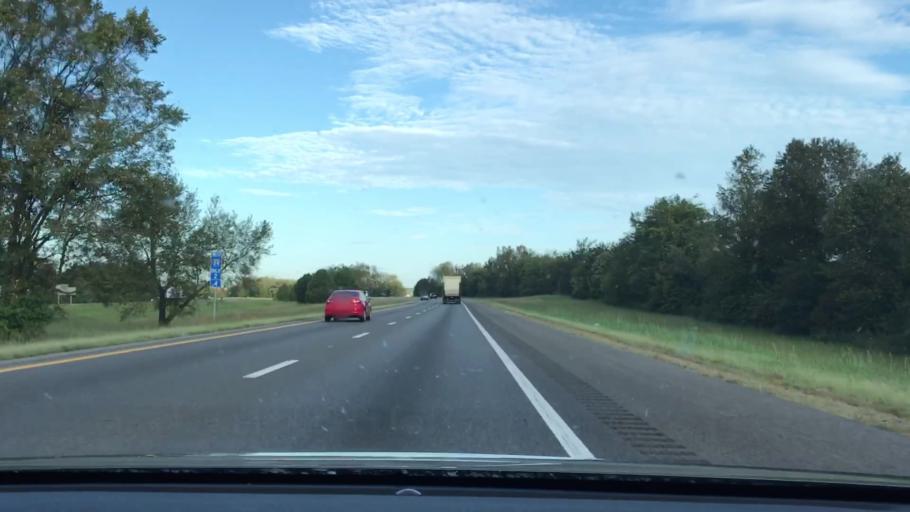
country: US
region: Tennessee
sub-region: Montgomery County
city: Clarksville
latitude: 36.6229
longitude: -87.3024
